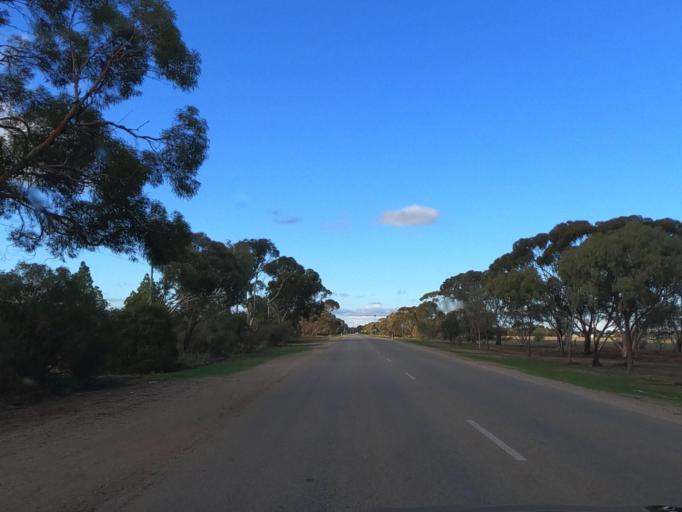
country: AU
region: Victoria
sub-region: Swan Hill
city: Swan Hill
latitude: -35.3454
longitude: 143.5245
